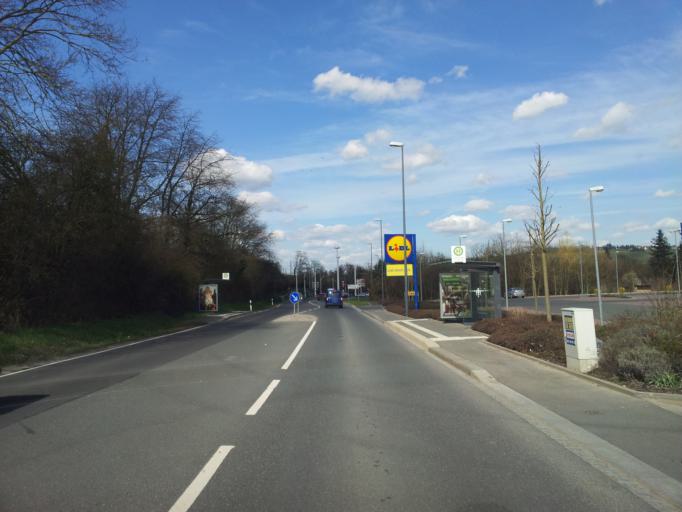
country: DE
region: Bavaria
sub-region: Regierungsbezirk Unterfranken
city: Reichenberg
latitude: 49.7564
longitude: 9.9426
